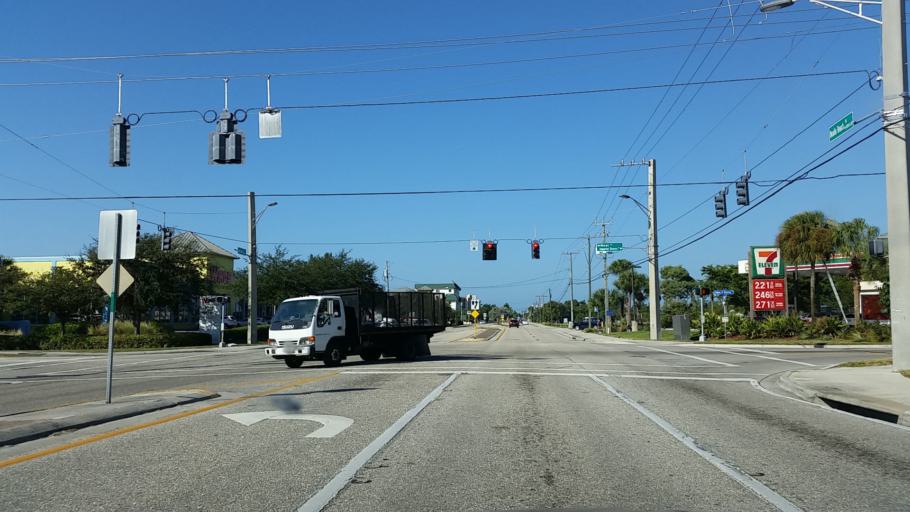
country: US
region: Florida
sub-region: Lee County
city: Bonita Springs
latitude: 26.3305
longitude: -81.8267
